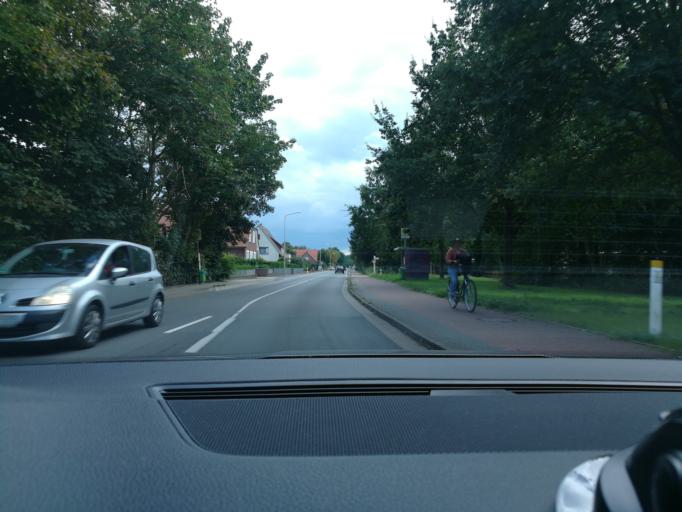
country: DE
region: North Rhine-Westphalia
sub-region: Regierungsbezirk Detmold
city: Minden
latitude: 52.3213
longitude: 8.8727
